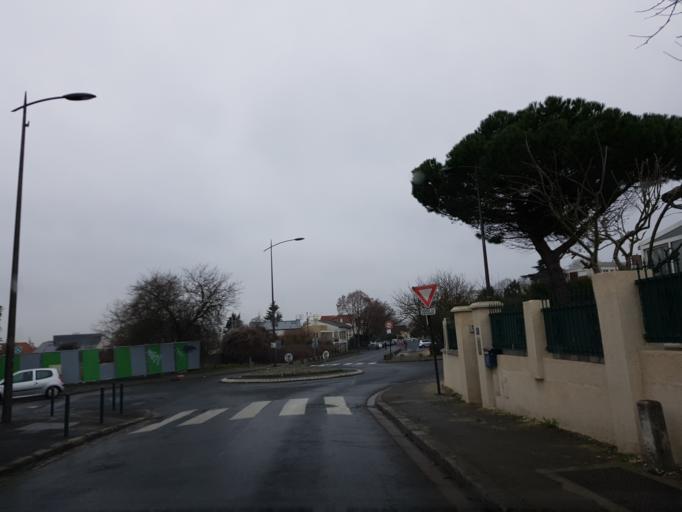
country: FR
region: Ile-de-France
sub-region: Departement du Val-de-Marne
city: Thiais
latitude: 48.7722
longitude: 2.3926
